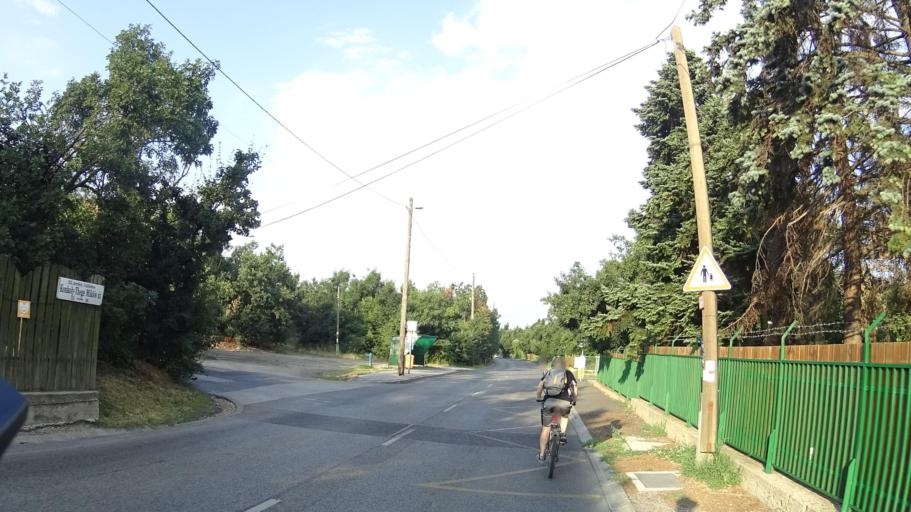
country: HU
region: Pest
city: Budaors
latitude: 47.4906
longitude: 18.9614
